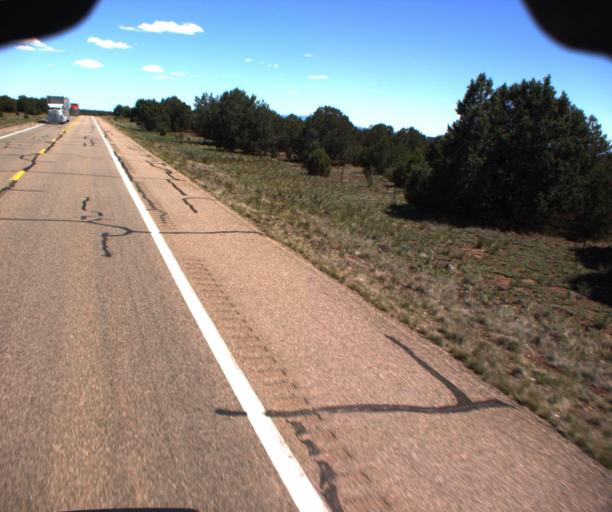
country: US
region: Arizona
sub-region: Yavapai County
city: Paulden
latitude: 35.0911
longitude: -112.4151
